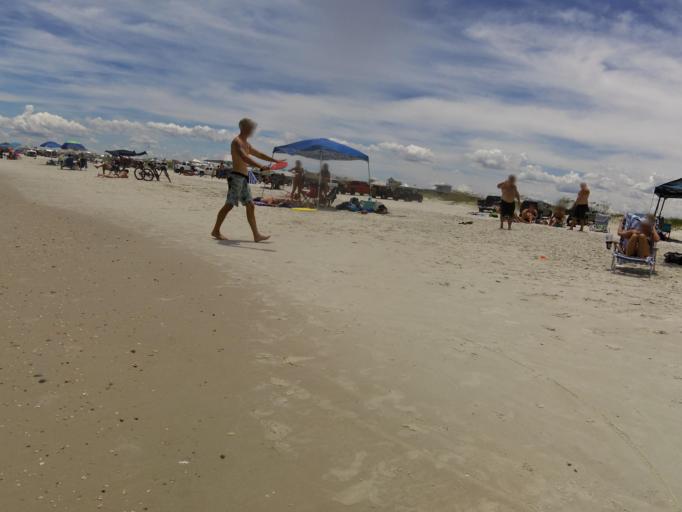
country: US
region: Florida
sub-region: Saint Johns County
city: Saint Augustine Beach
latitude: 29.8332
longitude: -81.2631
